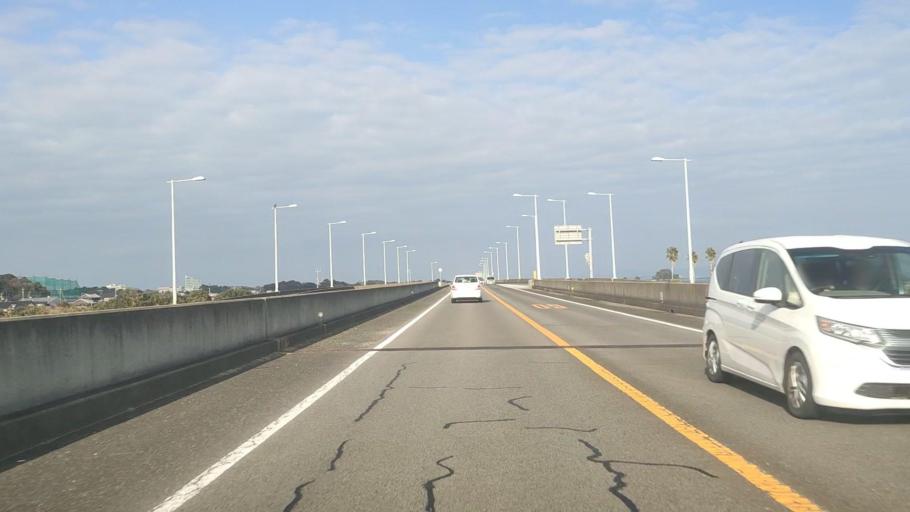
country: JP
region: Nagasaki
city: Shimabara
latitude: 32.7458
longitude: 130.3728
